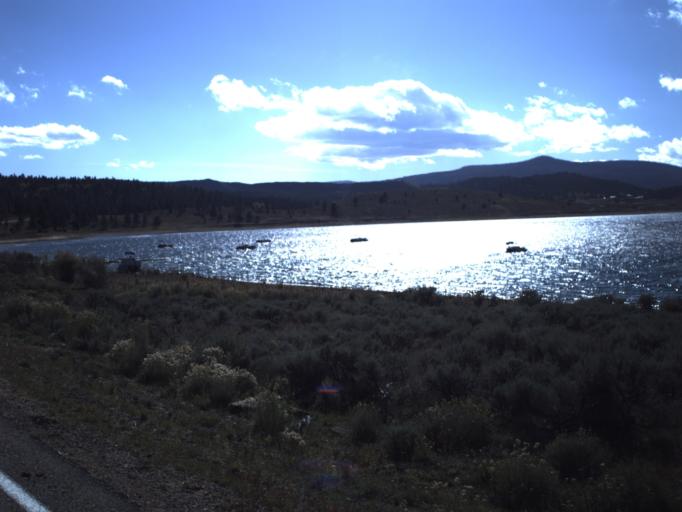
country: US
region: Utah
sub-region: Garfield County
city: Panguitch
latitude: 37.7158
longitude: -112.6227
